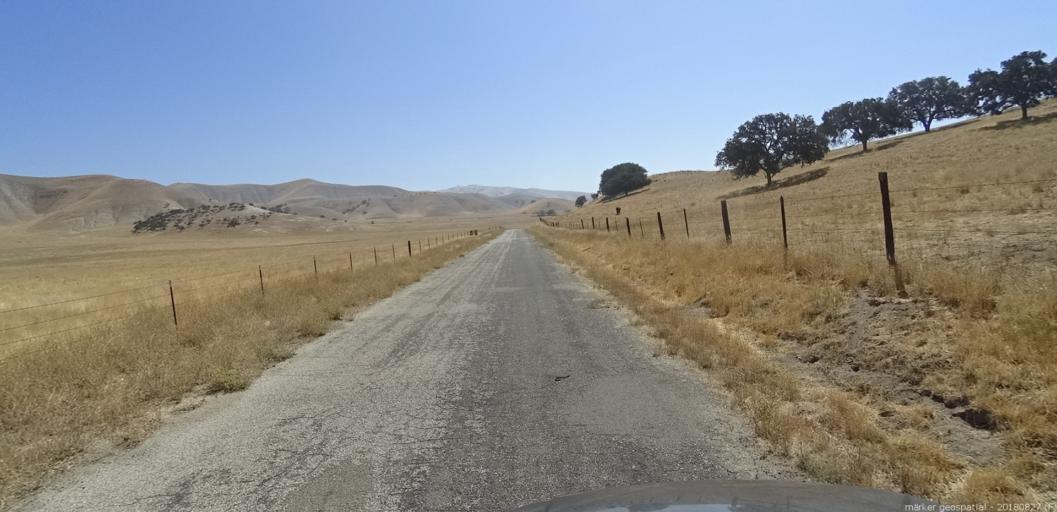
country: US
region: California
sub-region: Monterey County
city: King City
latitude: 36.2929
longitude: -120.9775
